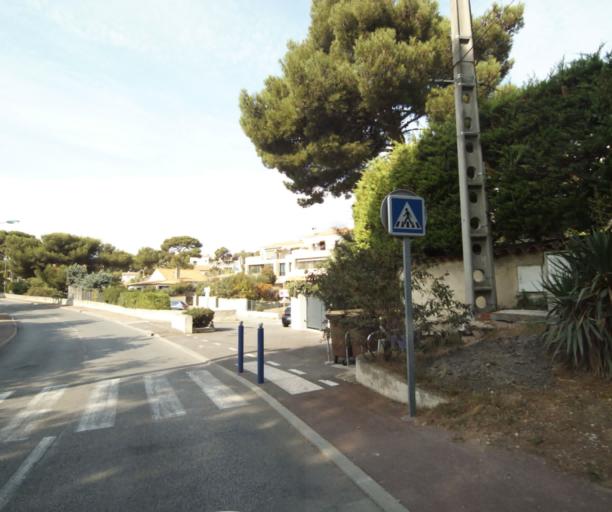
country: FR
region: Provence-Alpes-Cote d'Azur
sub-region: Departement des Bouches-du-Rhone
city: Sausset-les-Pins
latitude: 43.3305
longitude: 5.1269
